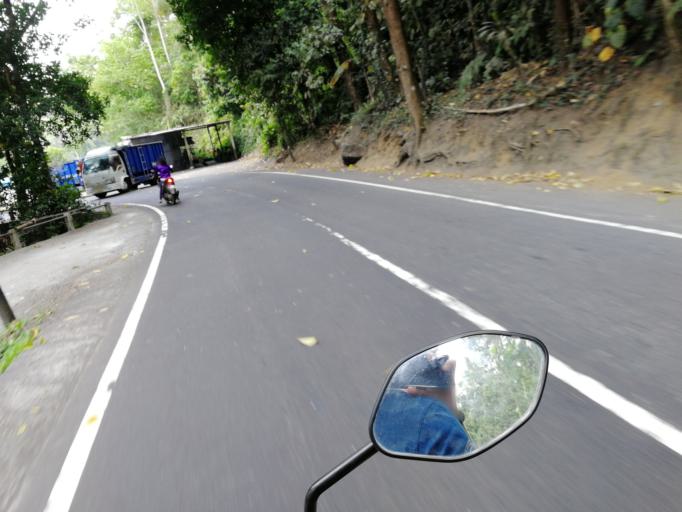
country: ID
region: Bali
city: Banjar Geriana Kangin
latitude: -8.4241
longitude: 115.4390
